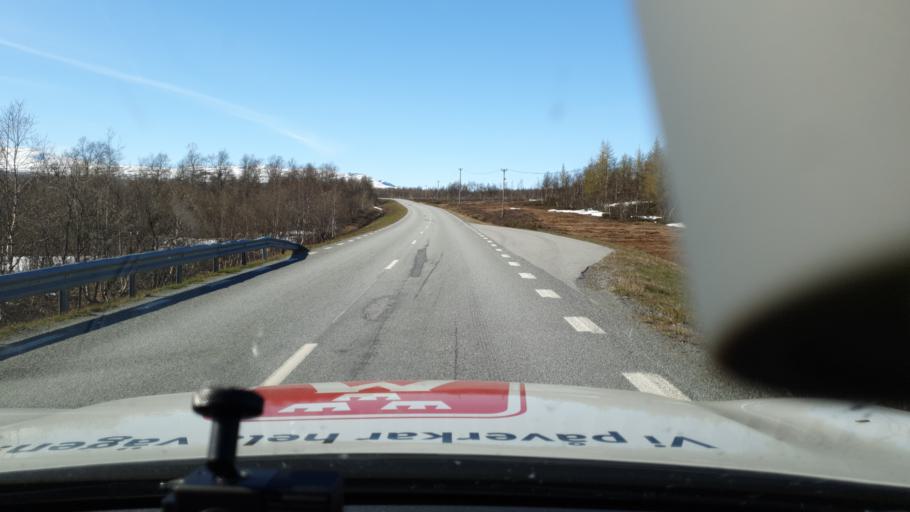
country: NO
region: Nordland
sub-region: Rana
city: Mo i Rana
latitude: 66.0230
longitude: 15.0860
